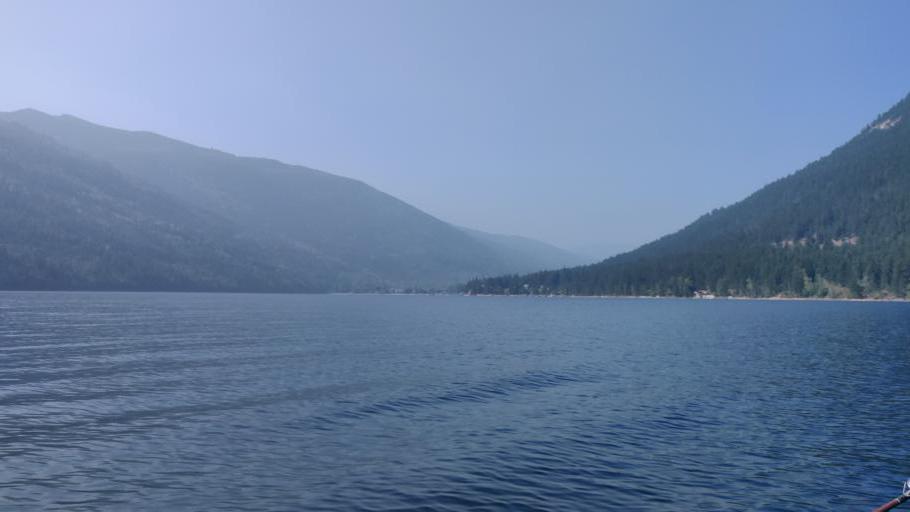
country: CA
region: British Columbia
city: Chase
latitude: 51.0715
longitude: -119.7566
